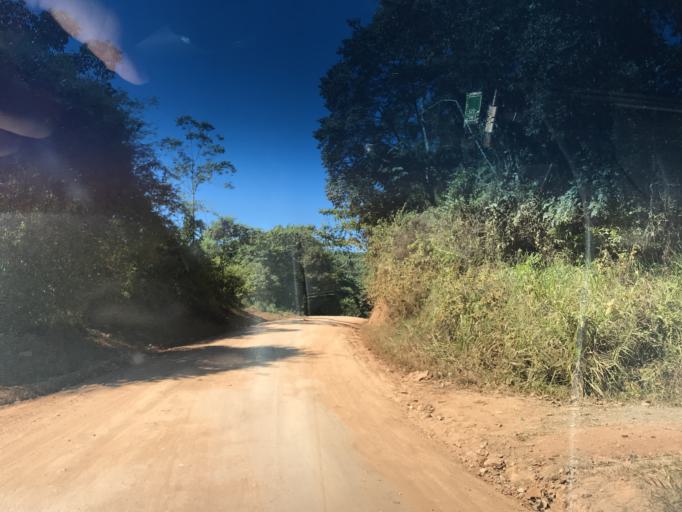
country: BR
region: Bahia
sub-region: Mutuipe
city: Mutuipe
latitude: -13.3737
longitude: -39.3796
